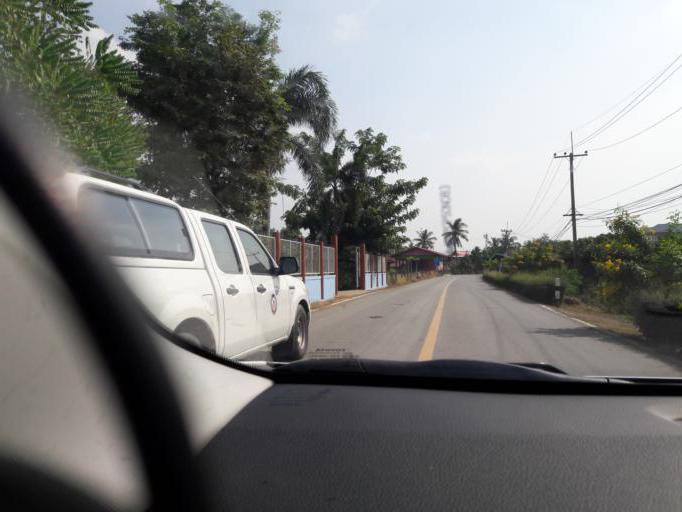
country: TH
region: Ang Thong
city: Pa Mok
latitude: 14.5348
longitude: 100.3935
